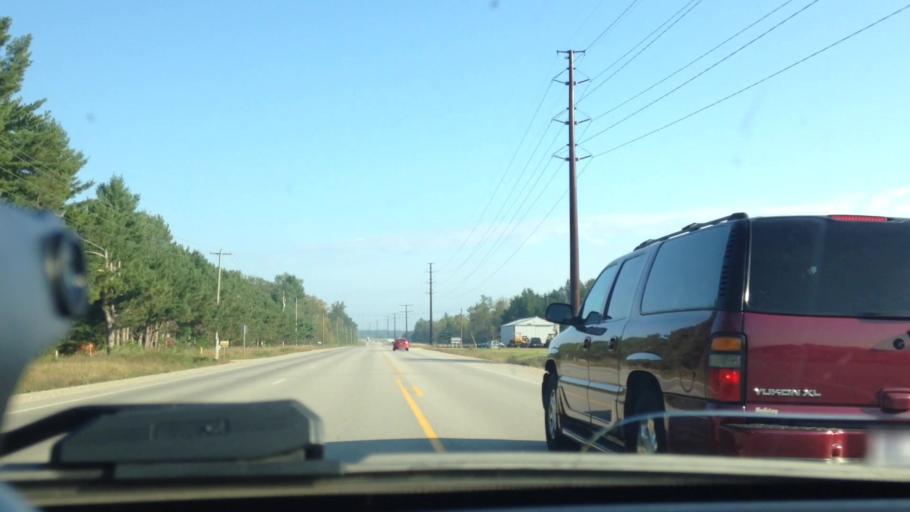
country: US
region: Wisconsin
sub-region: Marinette County
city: Peshtigo
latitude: 45.1876
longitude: -87.9952
